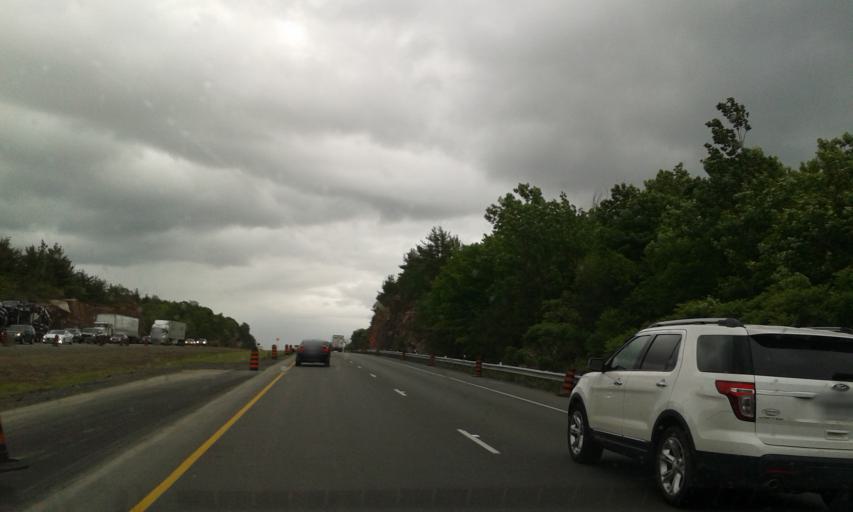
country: US
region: New York
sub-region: Jefferson County
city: Alexandria Bay
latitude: 44.3783
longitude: -76.0199
